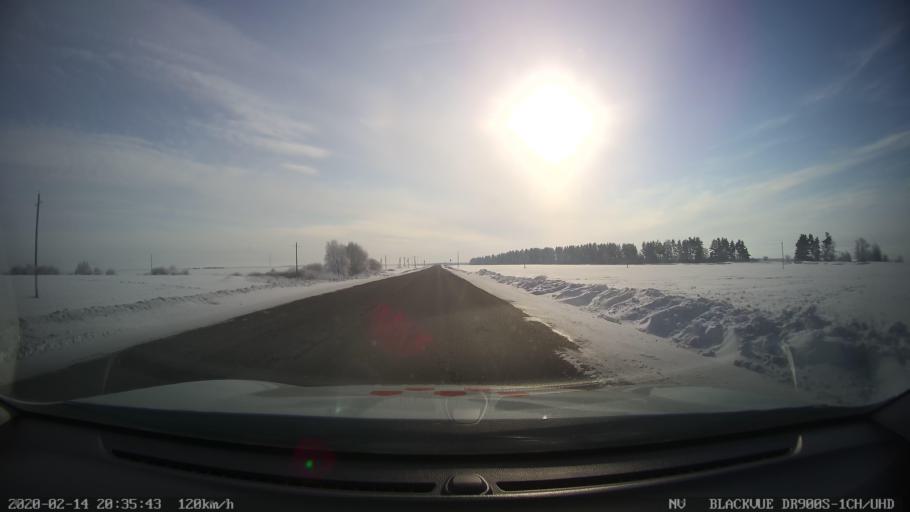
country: RU
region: Tatarstan
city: Kuybyshevskiy Zaton
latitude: 55.3783
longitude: 48.9891
